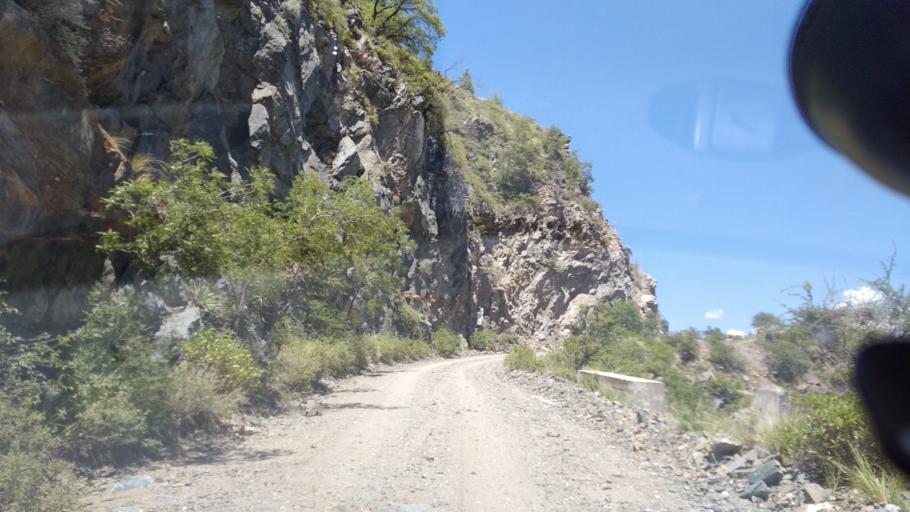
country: AR
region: Cordoba
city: Salsacate
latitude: -31.3723
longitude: -65.4066
